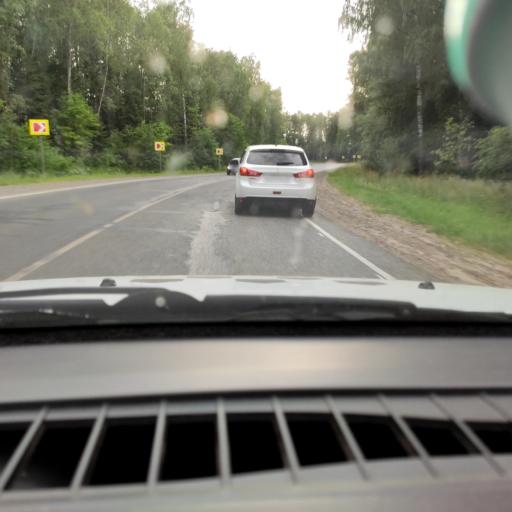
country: RU
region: Udmurtiya
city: Igra
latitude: 57.5863
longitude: 53.2397
